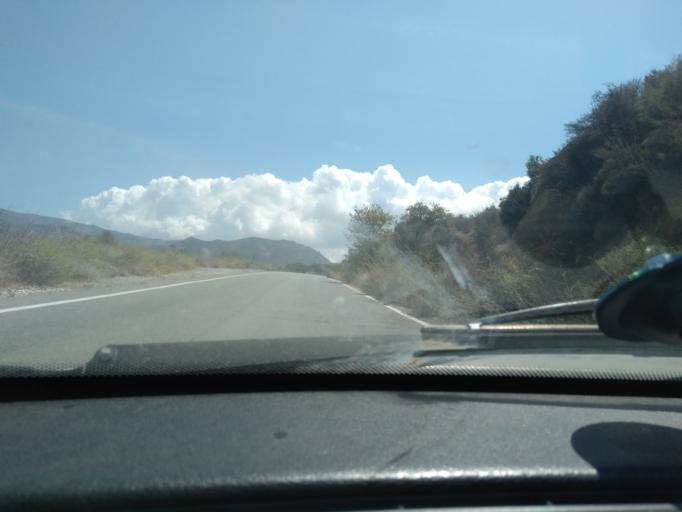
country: GR
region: Crete
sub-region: Nomos Lasithiou
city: Siteia
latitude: 35.1399
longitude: 26.0750
